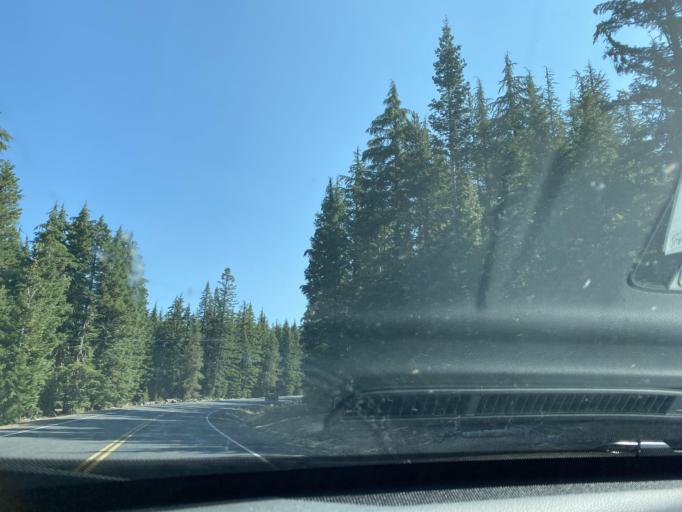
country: US
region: Oregon
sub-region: Deschutes County
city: Three Rivers
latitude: 43.7106
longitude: -121.2827
